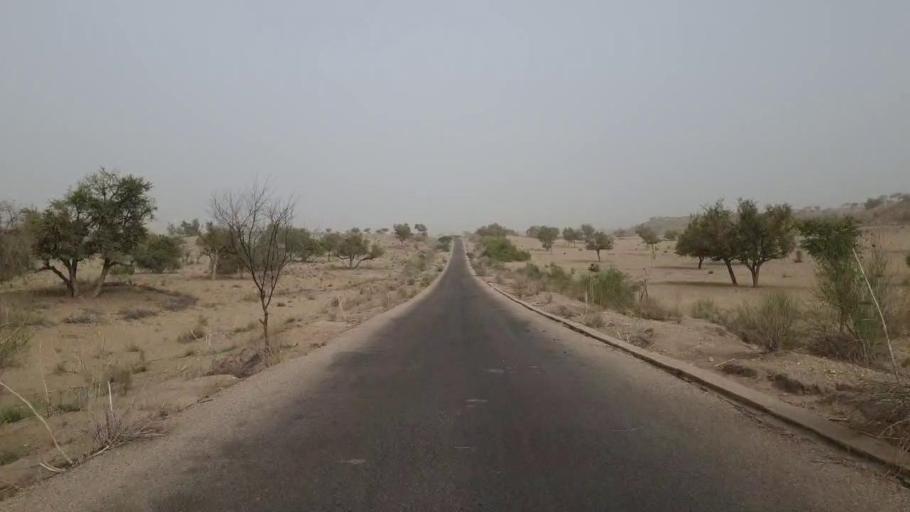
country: PK
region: Sindh
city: Islamkot
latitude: 24.5855
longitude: 70.2961
